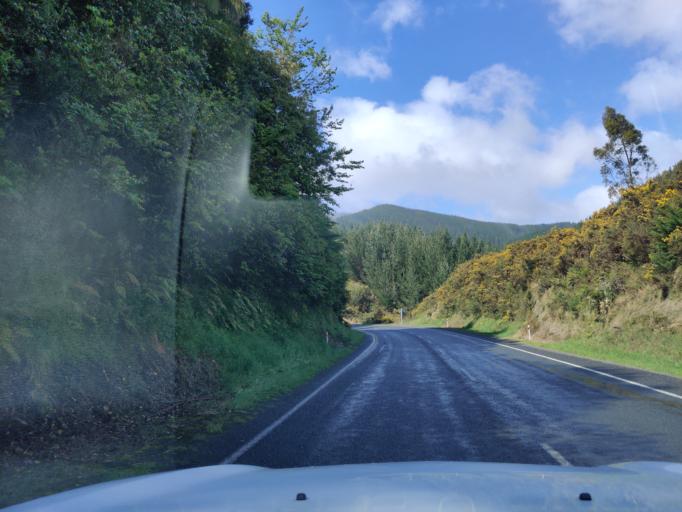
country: NZ
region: Bay of Plenty
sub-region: Rotorua District
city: Rotorua
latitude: -38.1634
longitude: 176.3070
